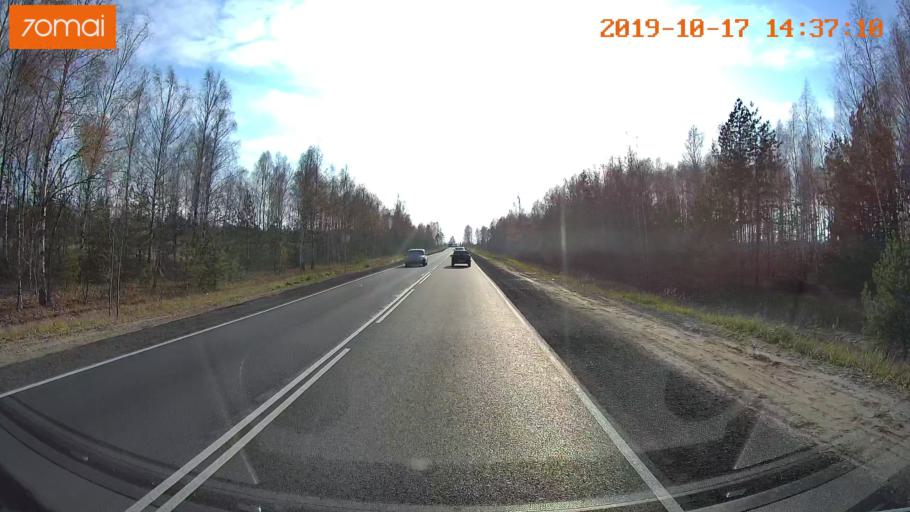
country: RU
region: Rjazan
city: Solotcha
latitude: 54.8826
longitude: 39.9984
